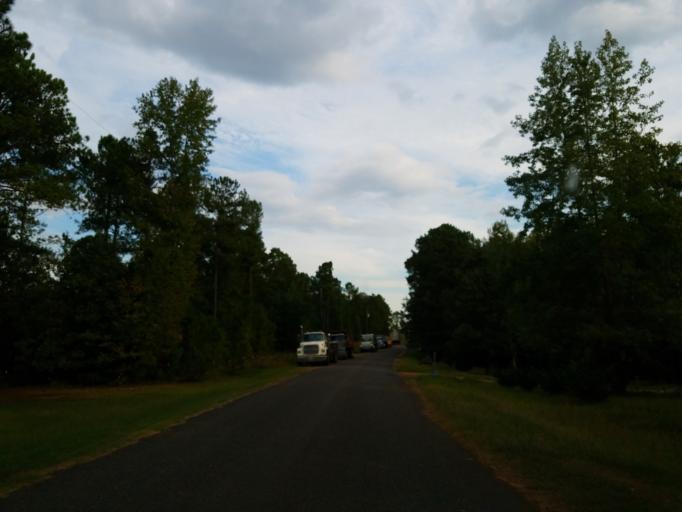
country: US
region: Georgia
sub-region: Monroe County
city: Forsyth
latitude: 33.1297
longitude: -84.0181
